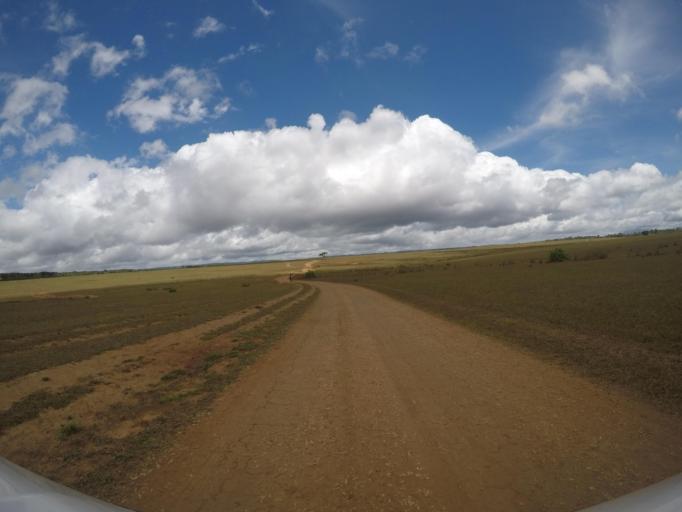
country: TL
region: Lautem
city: Lospalos
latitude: -8.4581
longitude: 126.9845
